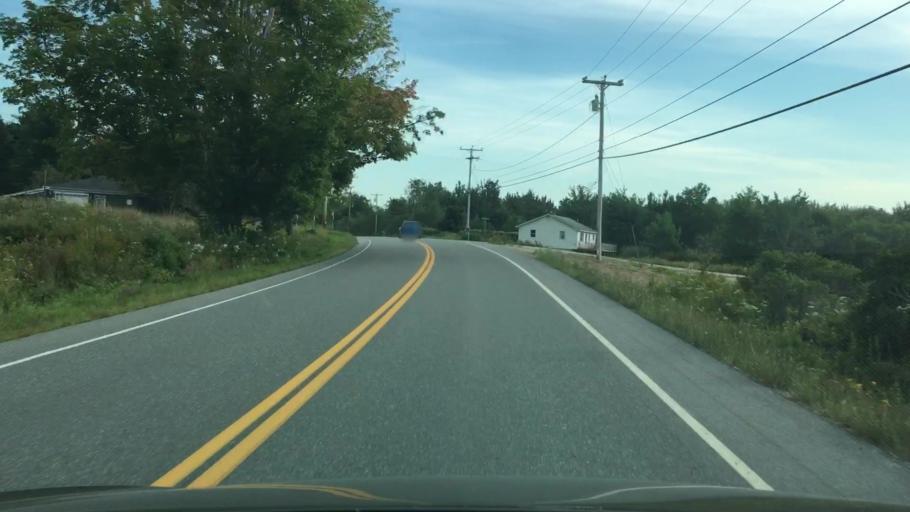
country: US
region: Maine
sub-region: Hancock County
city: Penobscot
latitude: 44.4711
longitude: -68.7816
